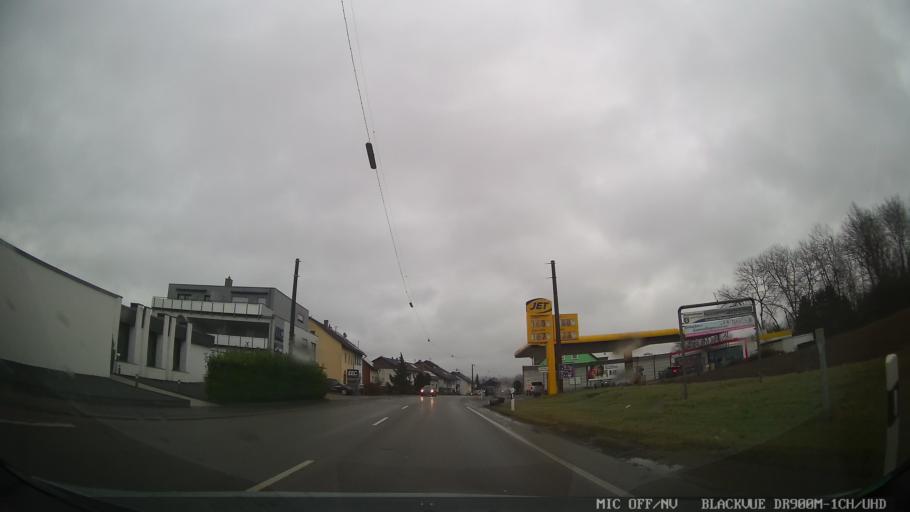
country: DE
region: Saarland
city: Saarwellingen
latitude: 49.3462
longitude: 6.7975
